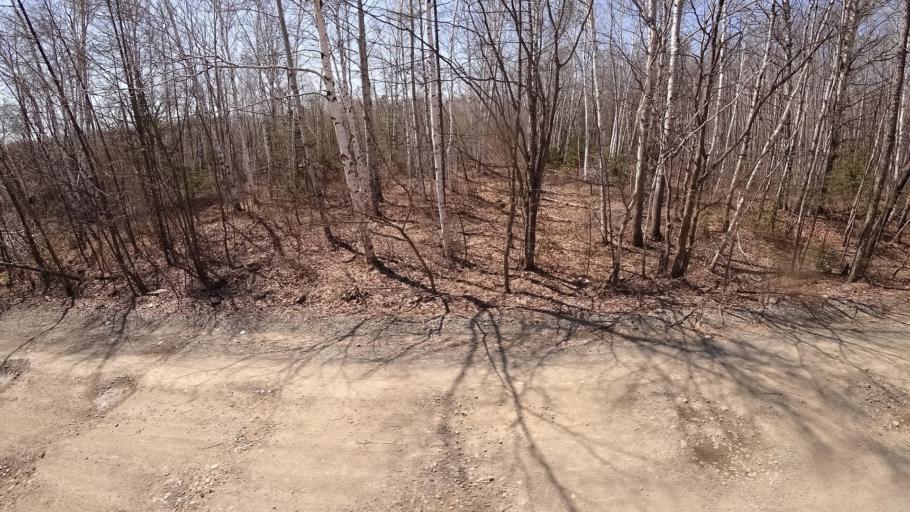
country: RU
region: Khabarovsk Krai
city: Khurba
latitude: 50.4129
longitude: 136.8423
